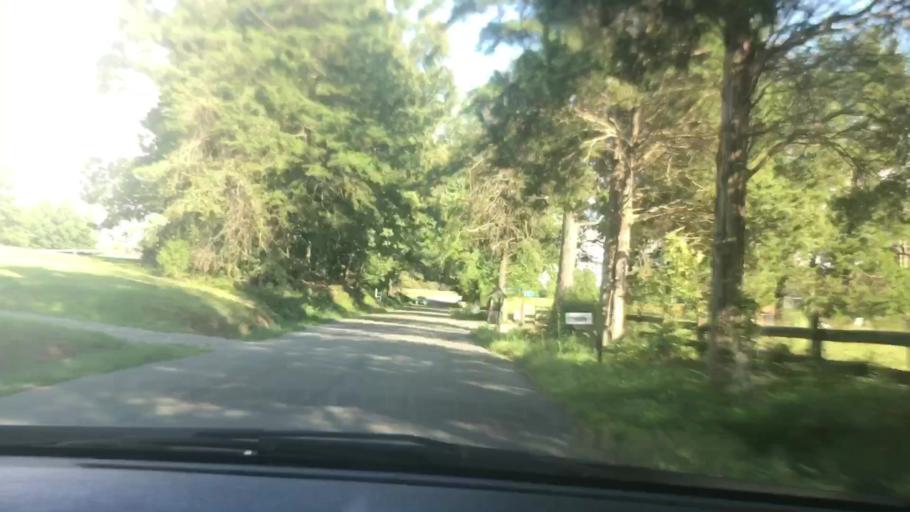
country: US
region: Virginia
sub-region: Henrico County
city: Short Pump
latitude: 37.6742
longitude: -77.7180
